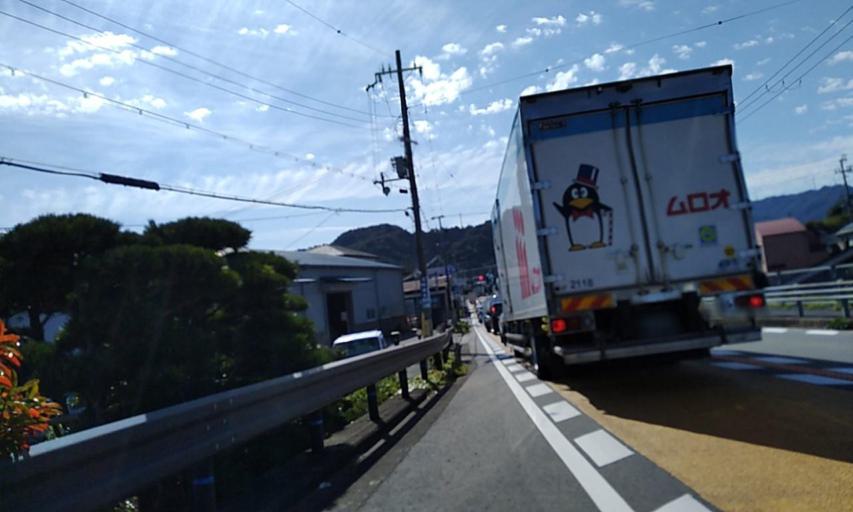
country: JP
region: Wakayama
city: Kainan
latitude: 34.0357
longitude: 135.1853
